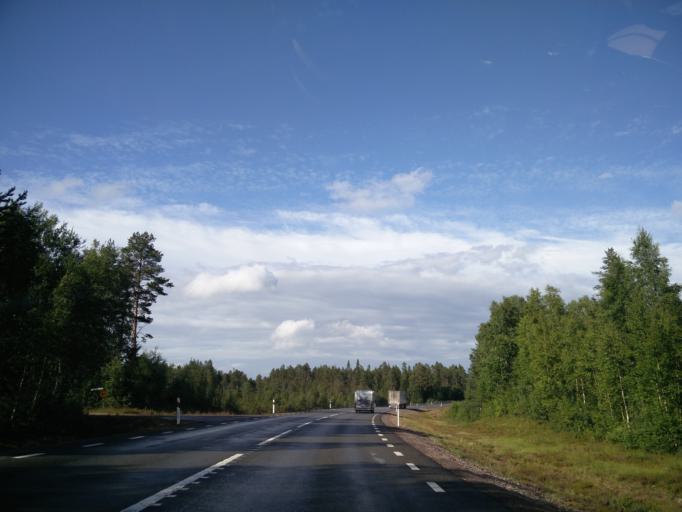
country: SE
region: Vaermland
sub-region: Hagfors Kommun
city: Ekshaerad
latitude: 60.4965
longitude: 13.4151
